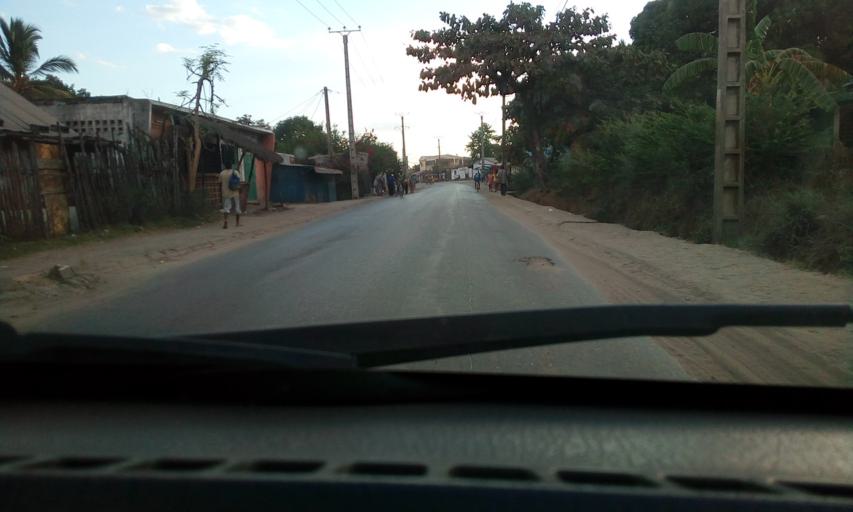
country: MG
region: Boeny
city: Mahajanga
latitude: -15.7150
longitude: 46.3372
